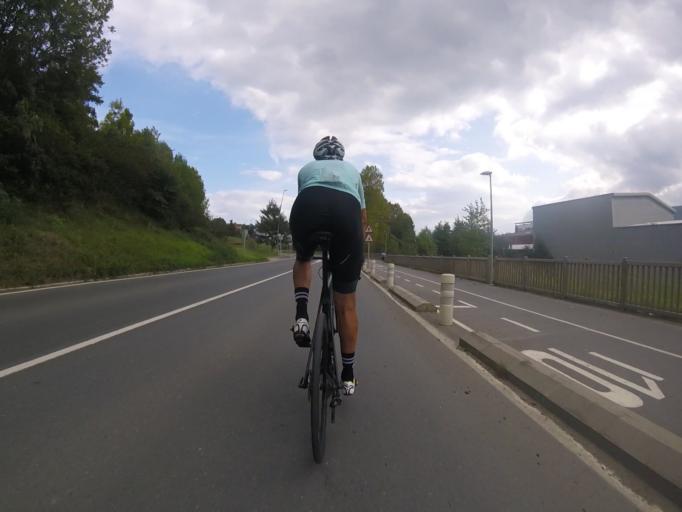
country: ES
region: Basque Country
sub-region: Provincia de Guipuzcoa
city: Aduna
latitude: 43.2075
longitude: -2.0396
